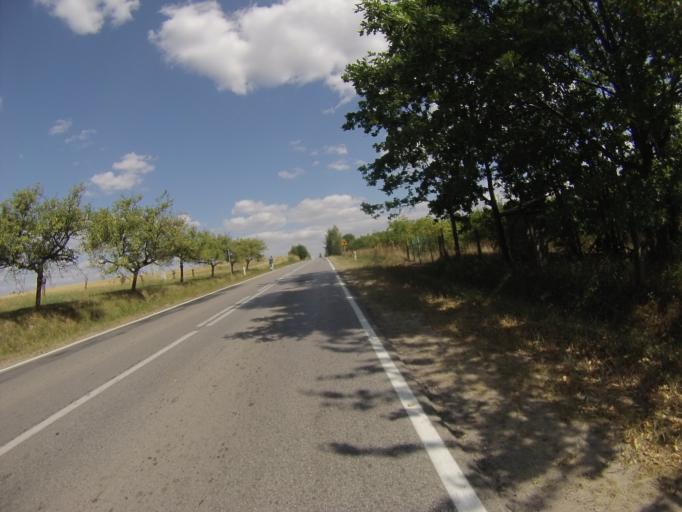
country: PL
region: Swietokrzyskie
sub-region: Powiat kielecki
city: Rakow
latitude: 50.7212
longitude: 21.0634
